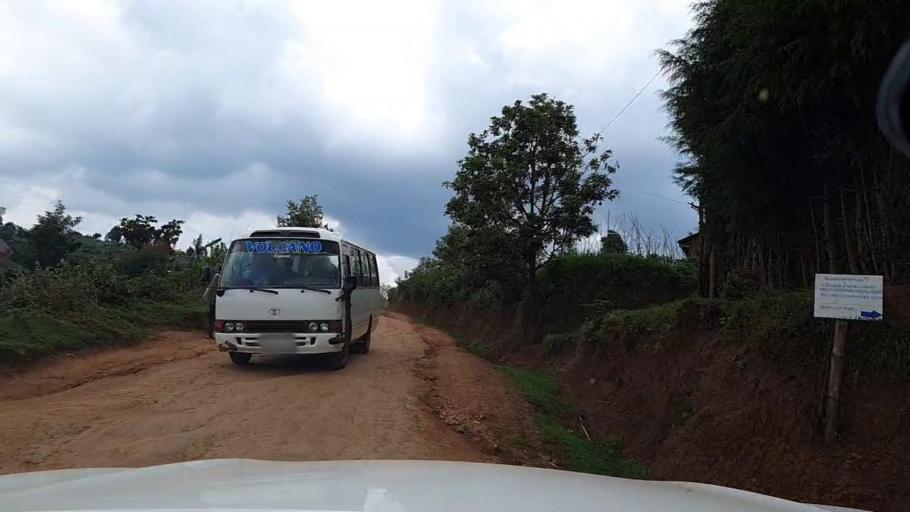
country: BI
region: Kayanza
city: Kayanza
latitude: -2.7112
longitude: 29.5312
